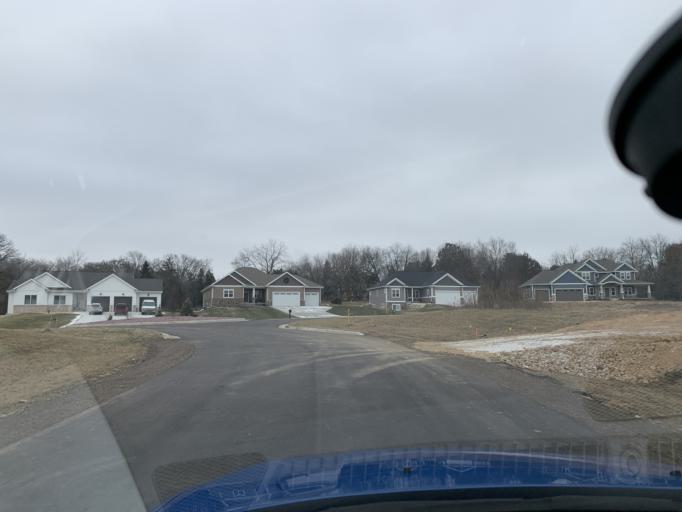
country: US
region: Wisconsin
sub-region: Dane County
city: Sun Prairie
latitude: 43.1964
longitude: -89.2680
